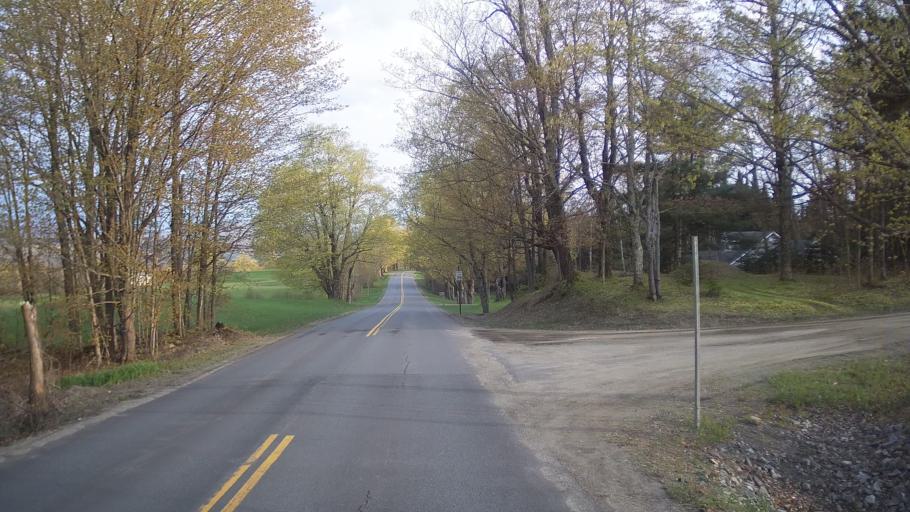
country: US
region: Vermont
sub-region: Orleans County
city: Newport
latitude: 44.9035
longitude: -72.4310
